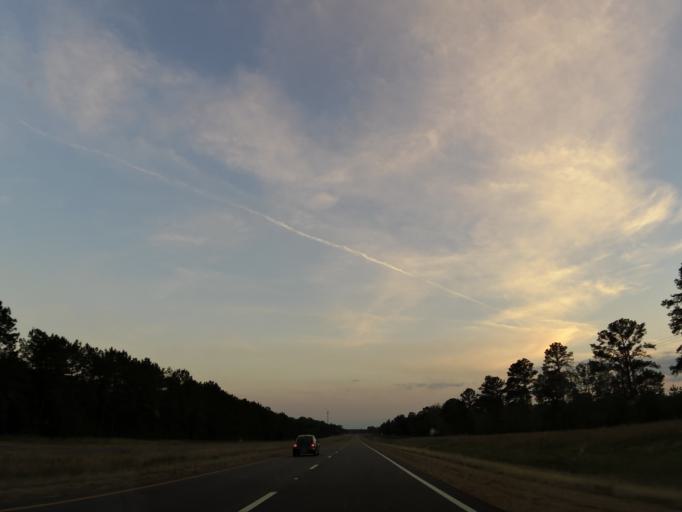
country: US
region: Mississippi
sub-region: Kemper County
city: De Kalb
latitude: 32.7847
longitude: -88.4593
